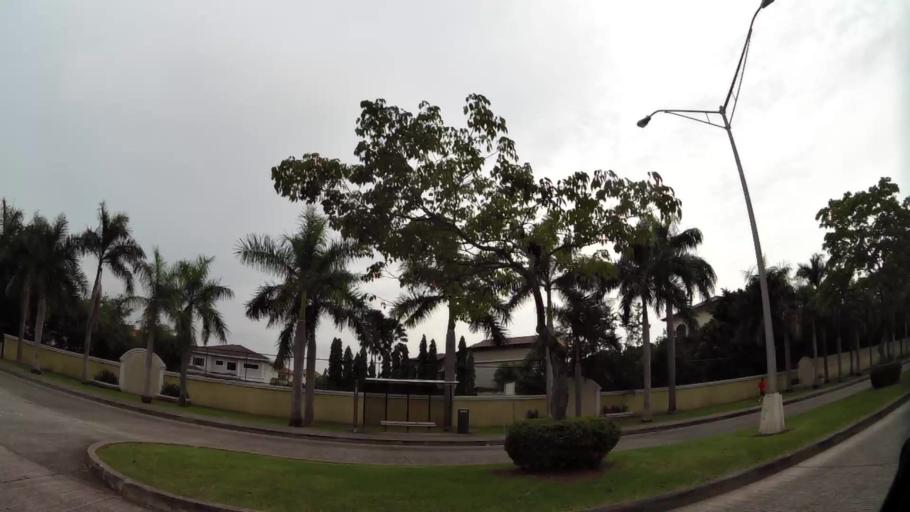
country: PA
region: Panama
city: San Miguelito
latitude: 9.0134
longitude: -79.4589
